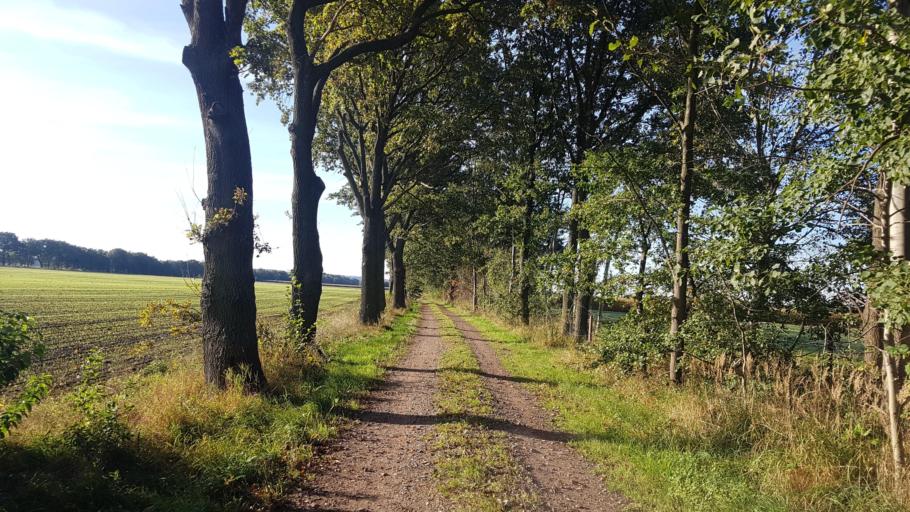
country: DE
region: Brandenburg
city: Tettau
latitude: 51.4310
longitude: 13.7180
